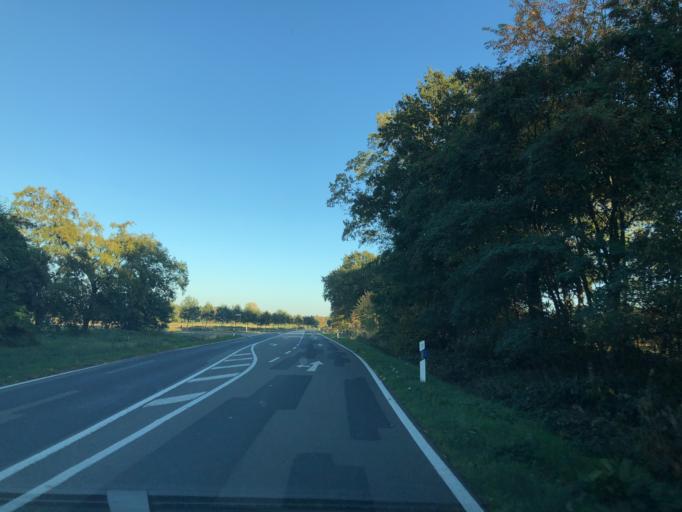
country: DE
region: Lower Saxony
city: Friesoythe
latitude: 53.0282
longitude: 7.7824
